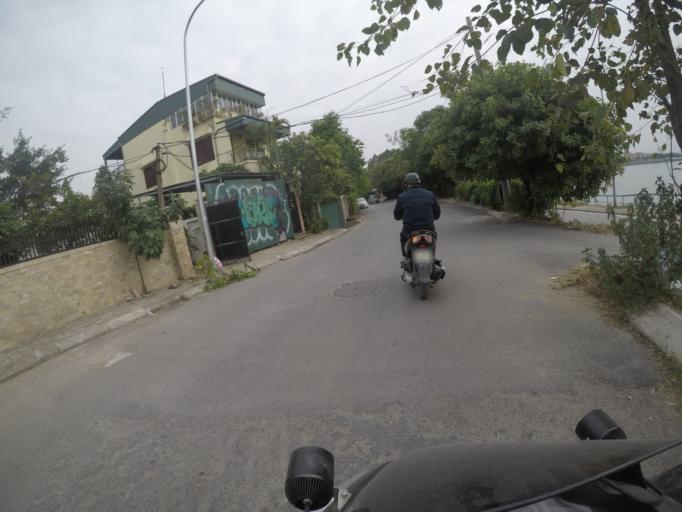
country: VN
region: Ha Noi
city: Tay Ho
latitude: 21.0727
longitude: 105.8215
